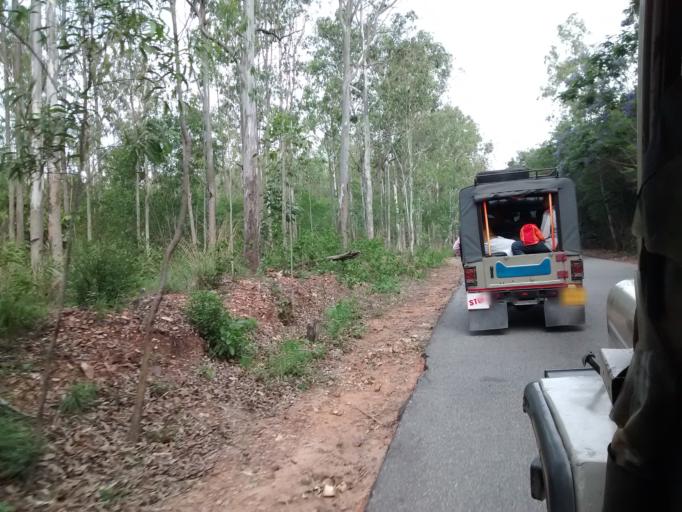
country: IN
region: Andhra Pradesh
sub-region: Chittoor
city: Tirumala
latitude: 13.7029
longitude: 79.3462
